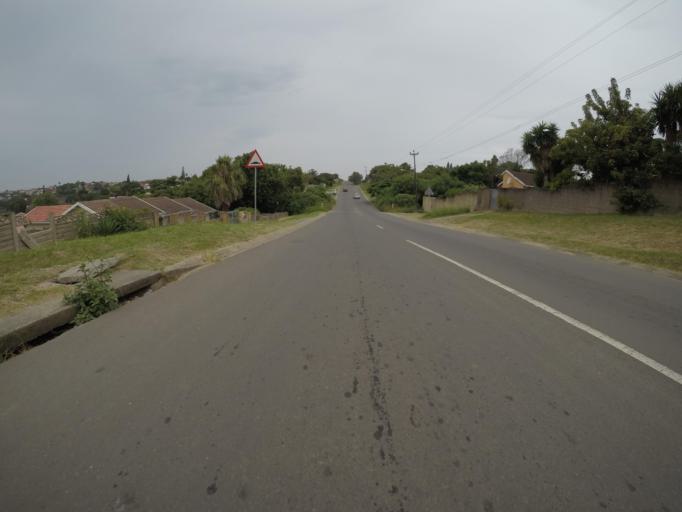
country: ZA
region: Eastern Cape
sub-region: Buffalo City Metropolitan Municipality
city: East London
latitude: -33.0028
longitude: 27.8540
